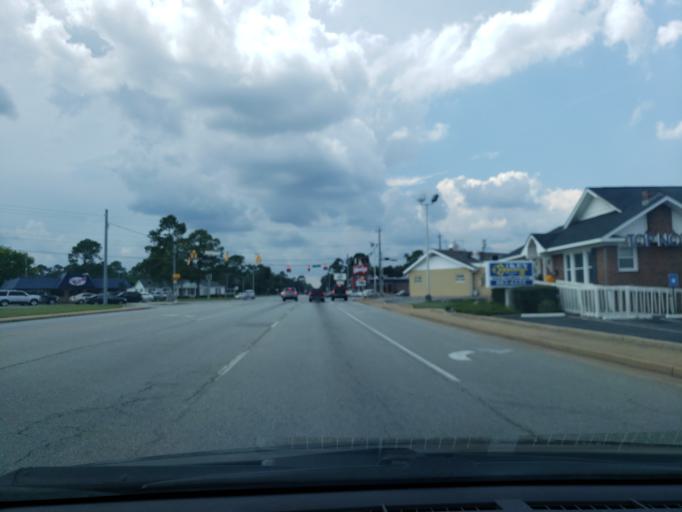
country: US
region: Georgia
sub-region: Dougherty County
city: Albany
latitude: 31.5810
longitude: -84.1754
